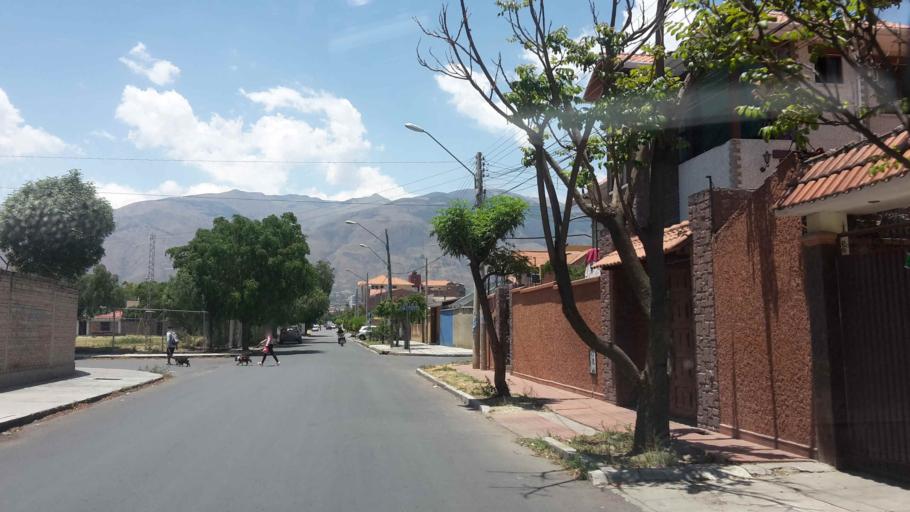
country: BO
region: Cochabamba
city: Cochabamba
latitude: -17.3805
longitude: -66.1916
